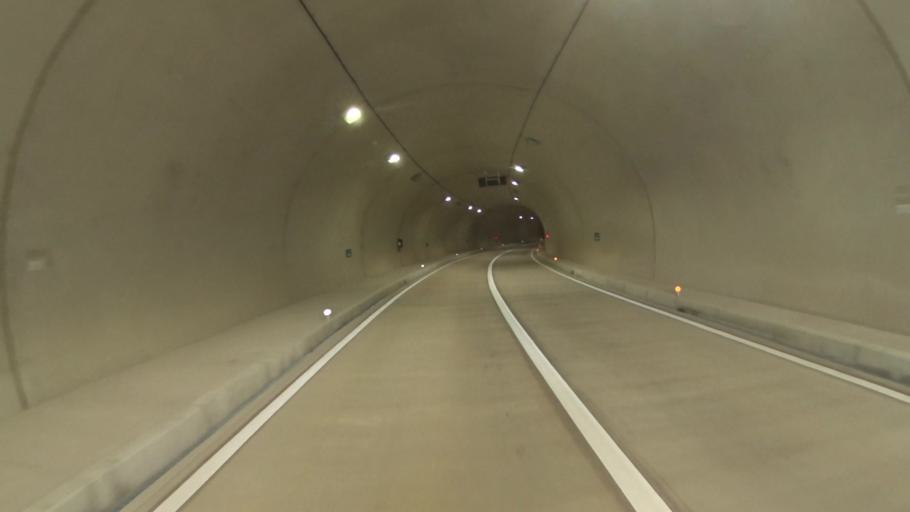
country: JP
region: Kyoto
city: Miyazu
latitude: 35.7444
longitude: 135.2559
